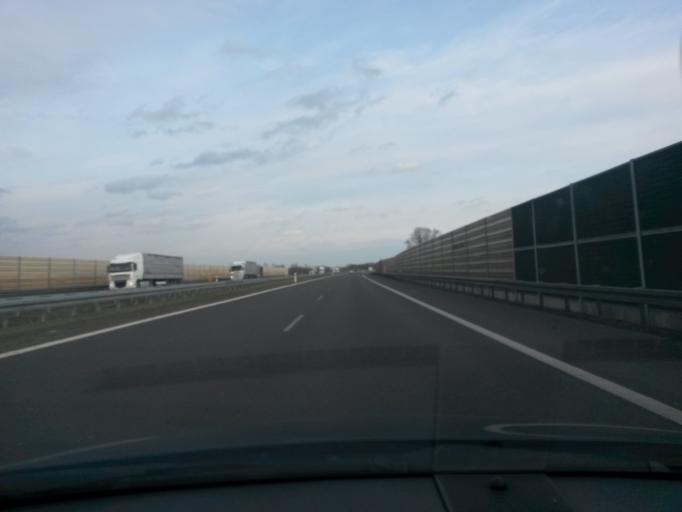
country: PL
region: Greater Poland Voivodeship
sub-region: Powiat turecki
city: Brudzew
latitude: 52.1297
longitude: 18.6584
